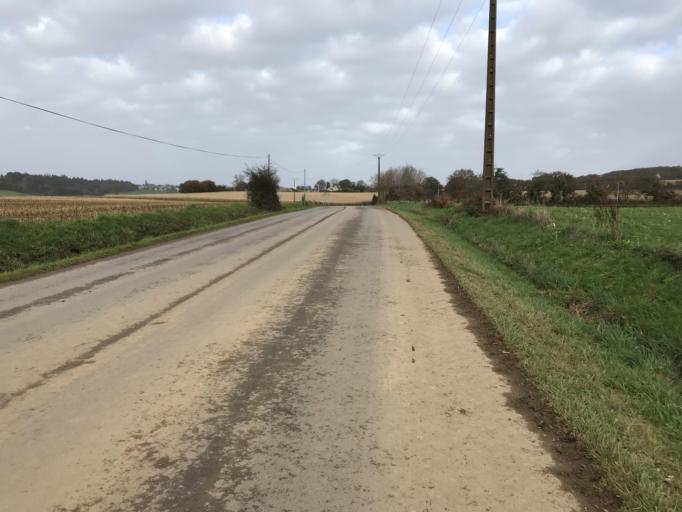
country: FR
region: Brittany
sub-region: Departement du Finistere
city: Irvillac
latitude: 48.3535
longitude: -4.2243
